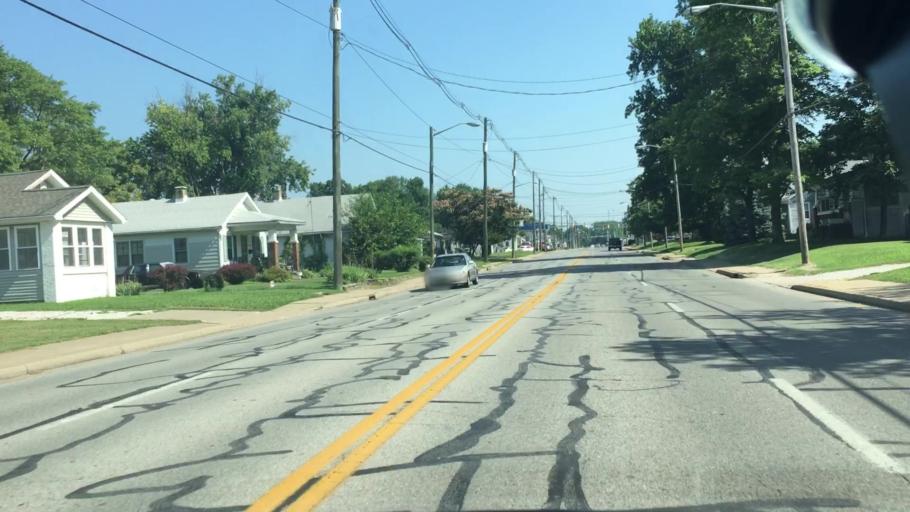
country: US
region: Indiana
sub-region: Vanderburgh County
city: Evansville
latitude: 37.9866
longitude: -87.5293
